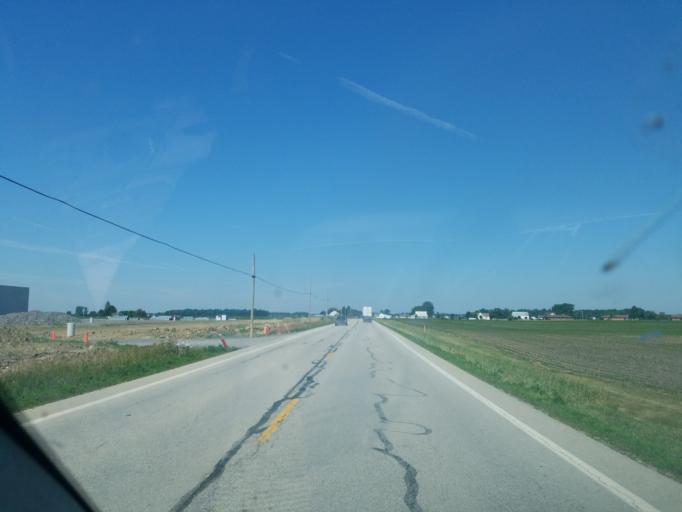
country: US
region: Ohio
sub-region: Shelby County
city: Jackson Center
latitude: 40.4397
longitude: -84.0624
